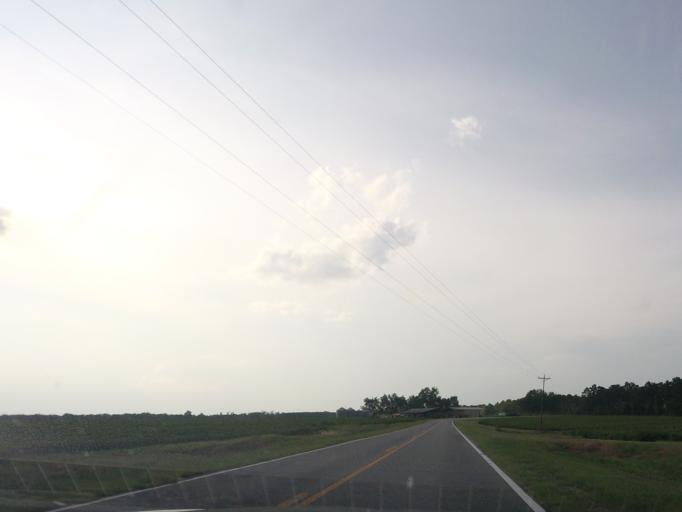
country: US
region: Georgia
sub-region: Bleckley County
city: Cochran
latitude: 32.4491
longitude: -83.2980
